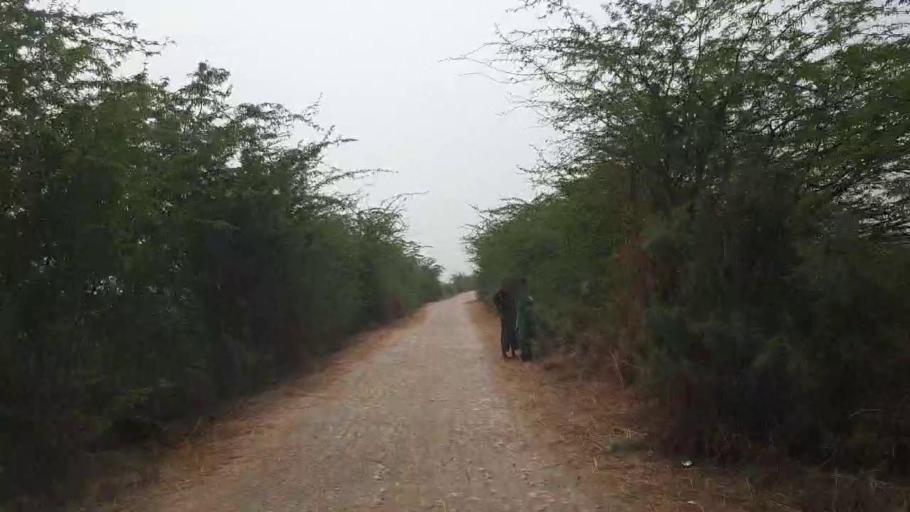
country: PK
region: Sindh
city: Kario
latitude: 24.6516
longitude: 68.6409
